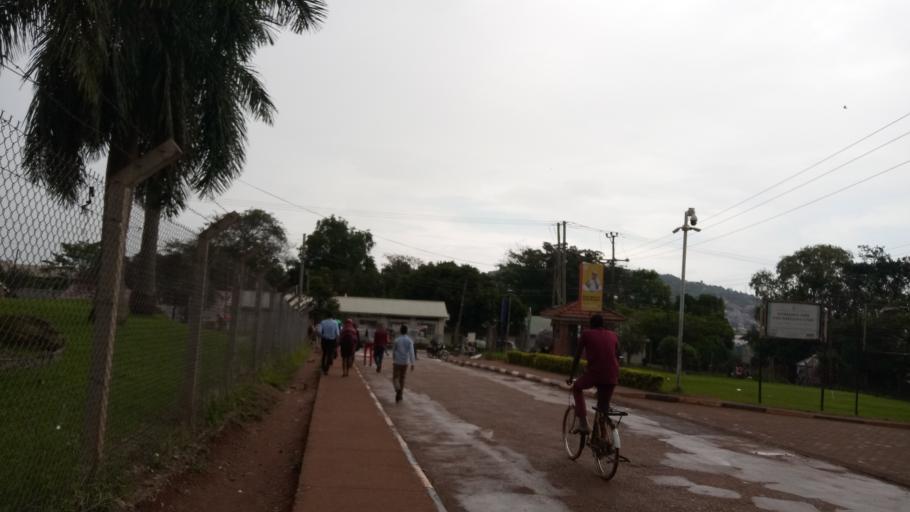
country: UG
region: Central Region
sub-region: Wakiso District
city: Kireka
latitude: 0.3459
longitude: 32.6325
